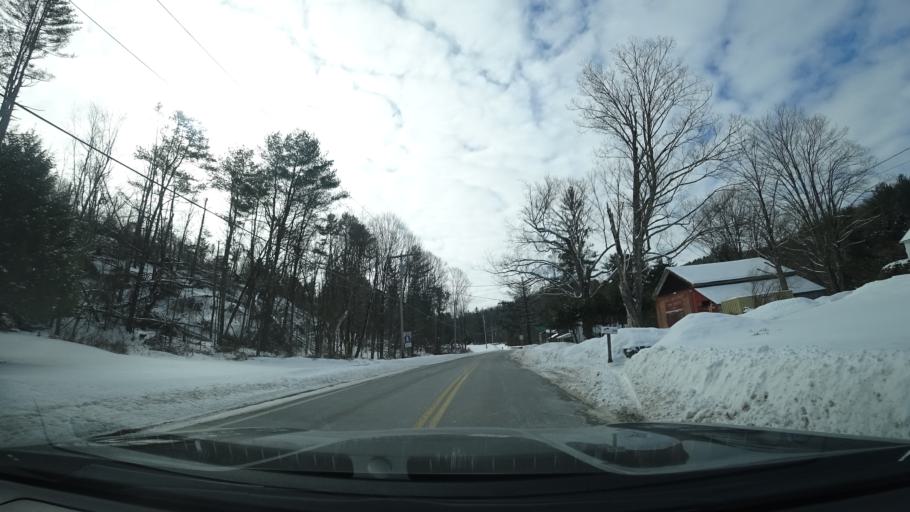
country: US
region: New York
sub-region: Washington County
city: Greenwich
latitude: 43.2378
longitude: -73.3772
